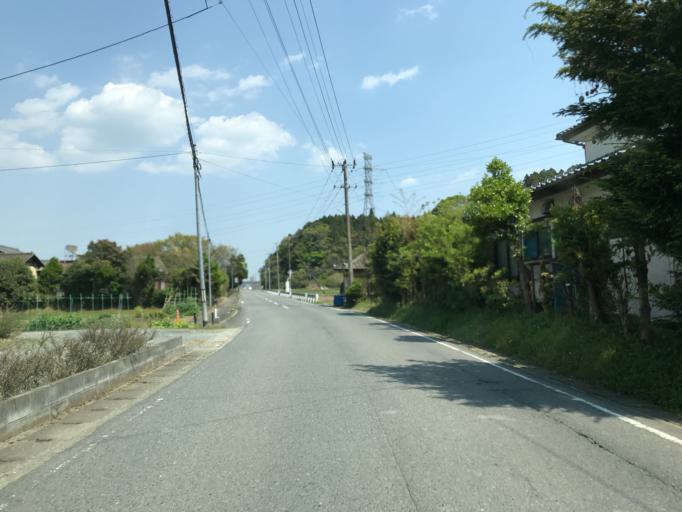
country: JP
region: Ibaraki
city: Kitaibaraki
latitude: 36.9179
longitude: 140.7503
